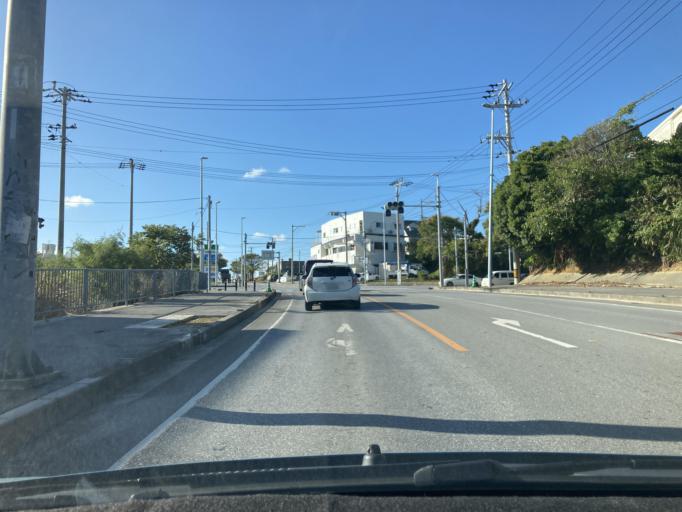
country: JP
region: Okinawa
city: Gushikawa
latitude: 26.3730
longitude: 127.8276
